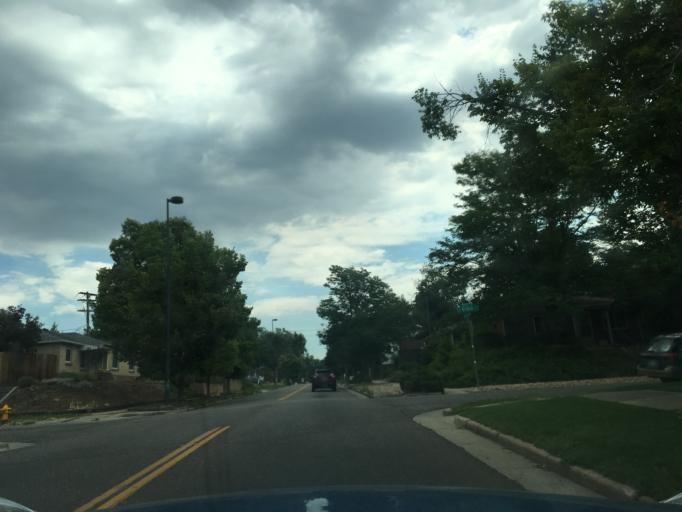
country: US
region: Colorado
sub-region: Denver County
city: Denver
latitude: 39.7111
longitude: -104.9679
